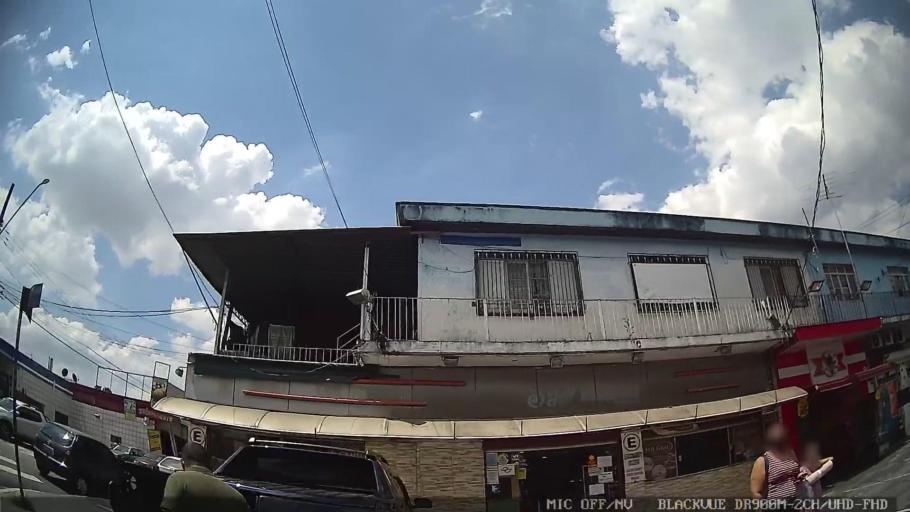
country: BR
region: Sao Paulo
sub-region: Ferraz De Vasconcelos
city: Ferraz de Vasconcelos
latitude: -23.5543
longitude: -46.4551
